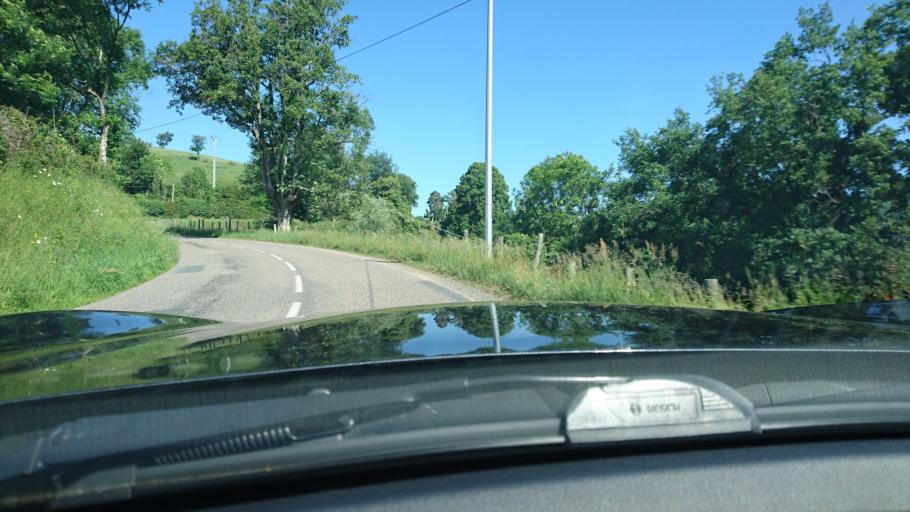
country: FR
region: Rhone-Alpes
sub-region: Departement du Rhone
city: Montrottier
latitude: 45.7873
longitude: 4.4879
